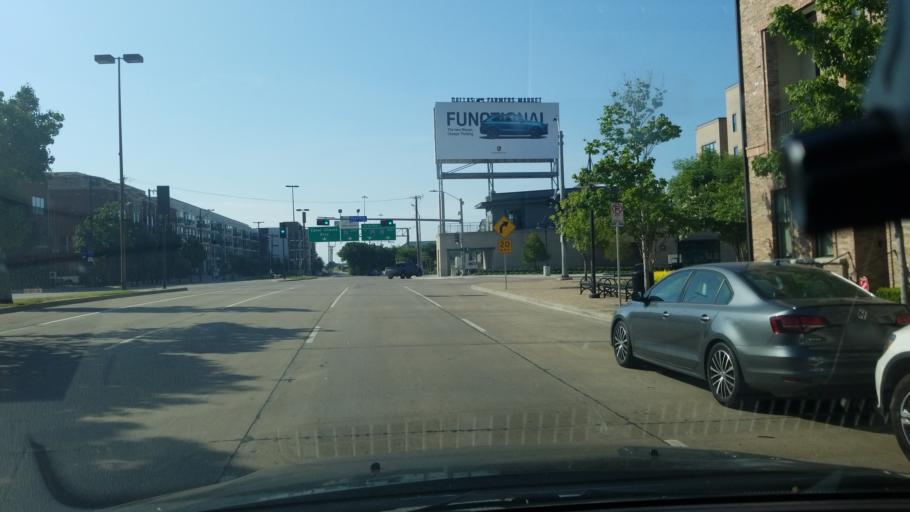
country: US
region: Texas
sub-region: Dallas County
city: Dallas
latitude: 32.7790
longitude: -96.7889
